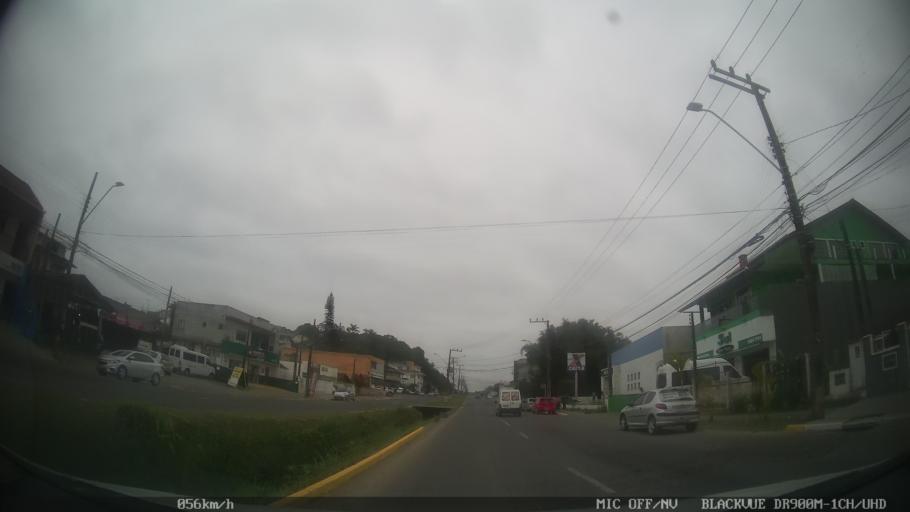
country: BR
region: Santa Catarina
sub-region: Joinville
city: Joinville
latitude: -26.3556
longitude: -48.8314
